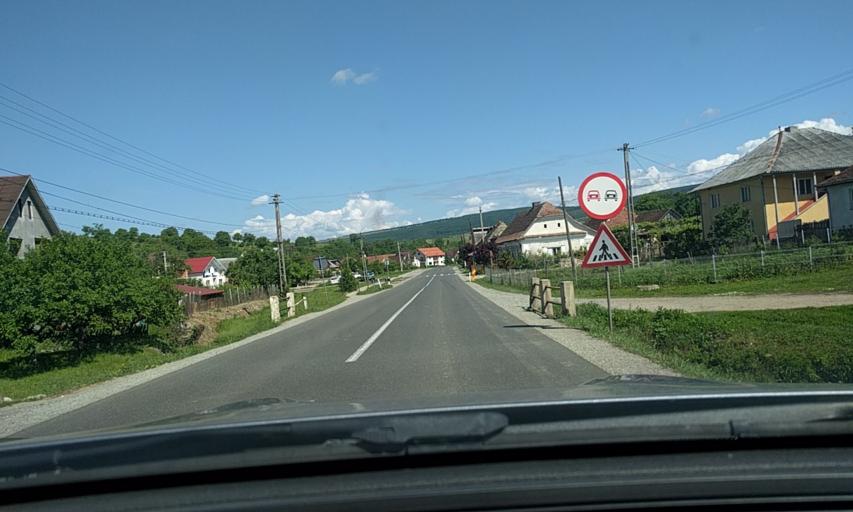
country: RO
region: Bistrita-Nasaud
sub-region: Comuna Dumitra
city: Dumitra
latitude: 47.2150
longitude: 24.4681
